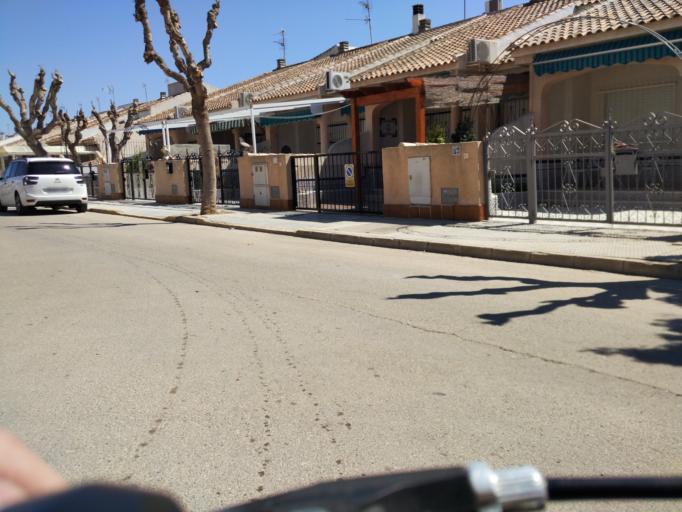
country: ES
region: Murcia
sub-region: Murcia
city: Los Alcazares
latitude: 37.7481
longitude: -0.8517
